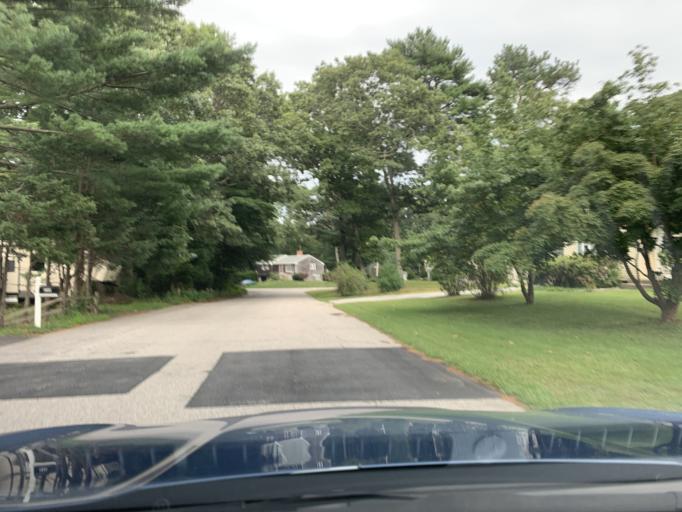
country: US
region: Rhode Island
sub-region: Kent County
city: East Greenwich
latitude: 41.6196
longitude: -71.4475
